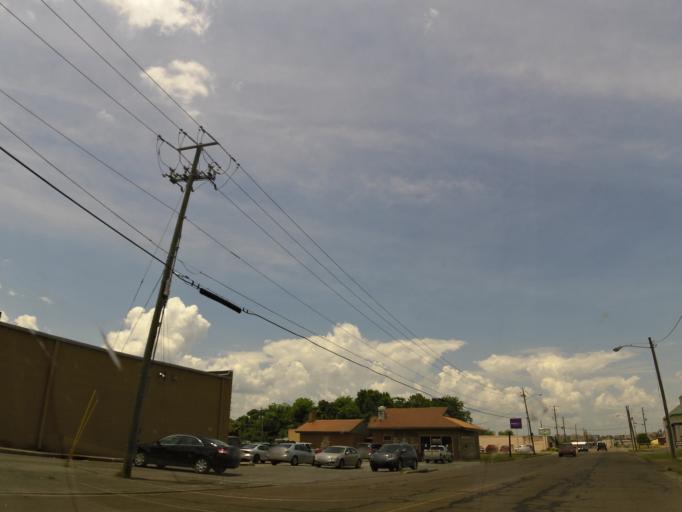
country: US
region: Mississippi
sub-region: Lauderdale County
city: Meridian
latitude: 32.3567
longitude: -88.6880
